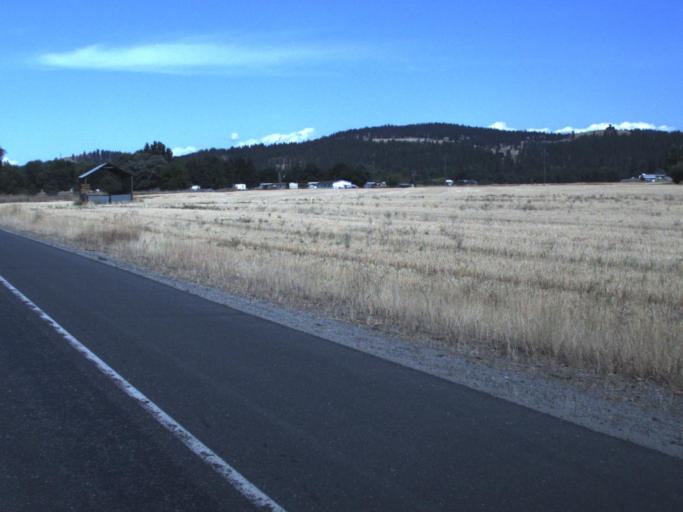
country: US
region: Washington
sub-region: Stevens County
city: Colville
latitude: 48.4482
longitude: -117.8726
